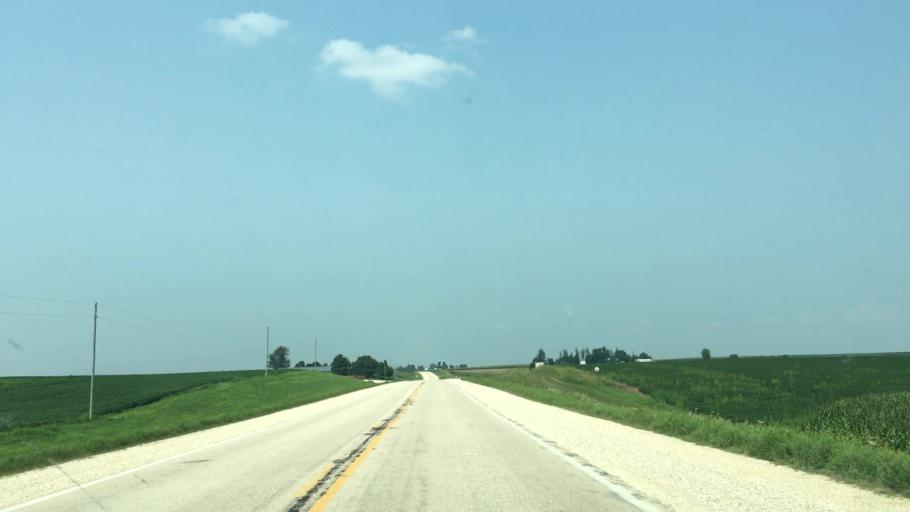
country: US
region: Iowa
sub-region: Fayette County
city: West Union
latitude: 42.9872
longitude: -91.8241
